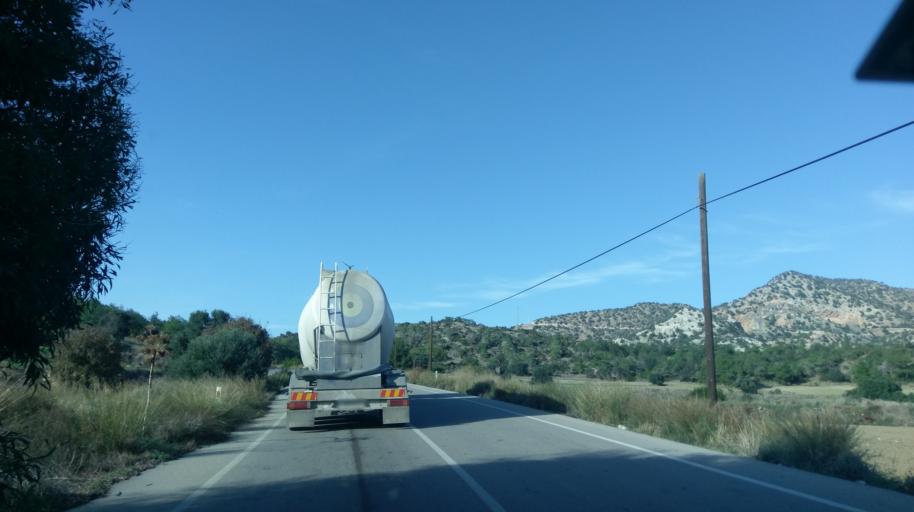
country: CY
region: Ammochostos
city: Lefkonoiko
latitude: 35.3355
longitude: 33.7199
